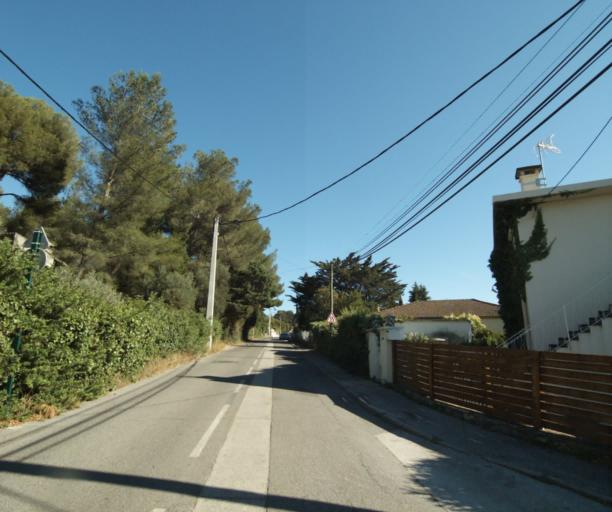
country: FR
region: Provence-Alpes-Cote d'Azur
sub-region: Departement du Var
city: La Garde
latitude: 43.1096
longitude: 5.9910
